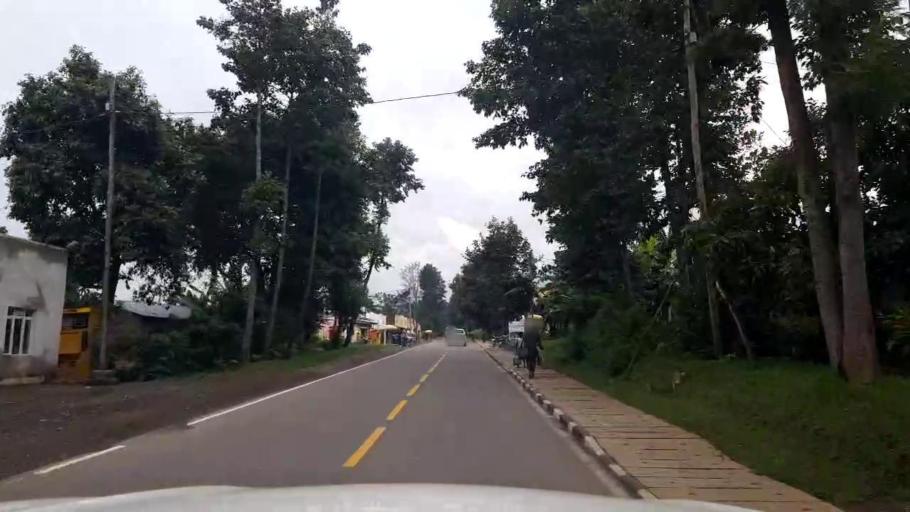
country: RW
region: Northern Province
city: Musanze
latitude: -1.4605
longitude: 29.6130
